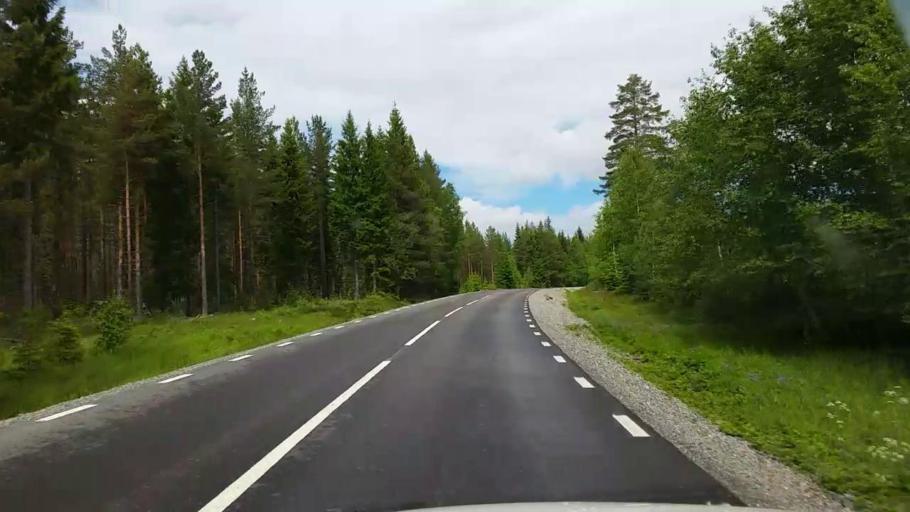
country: SE
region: Gaevleborg
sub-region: Sandvikens Kommun
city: Jarbo
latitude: 60.8978
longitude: 16.3758
